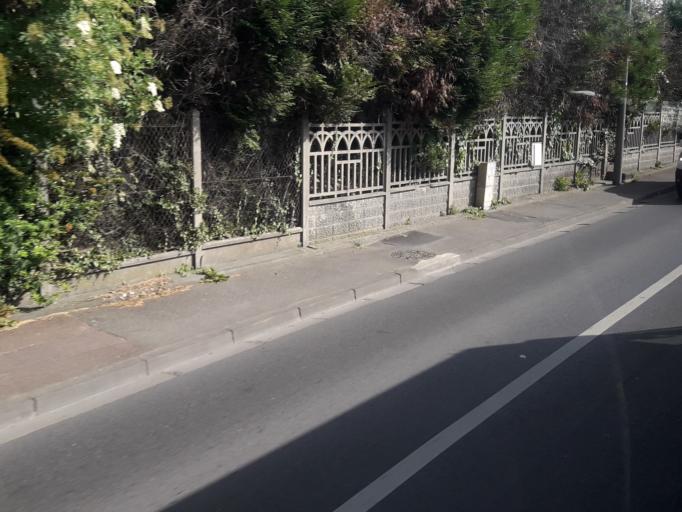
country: FR
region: Ile-de-France
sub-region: Departement de l'Essonne
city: Champlan
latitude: 48.6947
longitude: 2.2889
